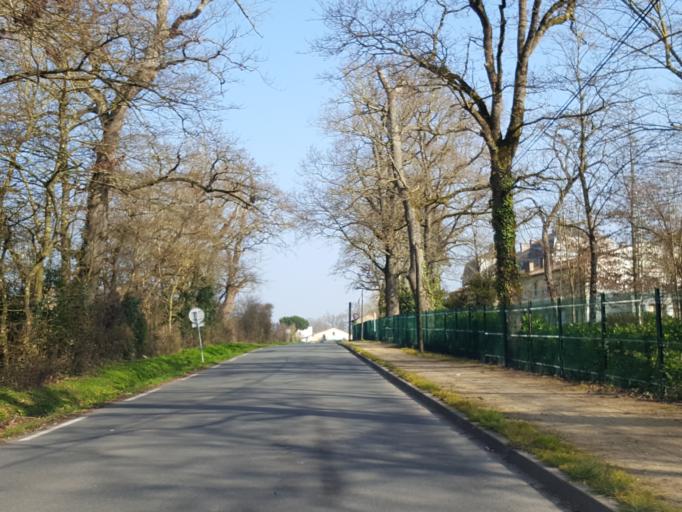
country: FR
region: Pays de la Loire
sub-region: Departement de la Vendee
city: La Roche-sur-Yon
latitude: 46.6717
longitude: -1.4508
